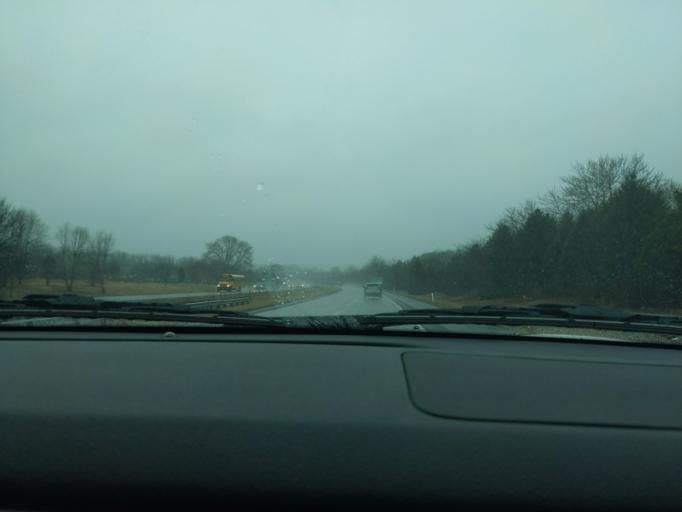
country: US
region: Pennsylvania
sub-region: Bucks County
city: Doylestown
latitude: 40.3143
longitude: -75.1476
